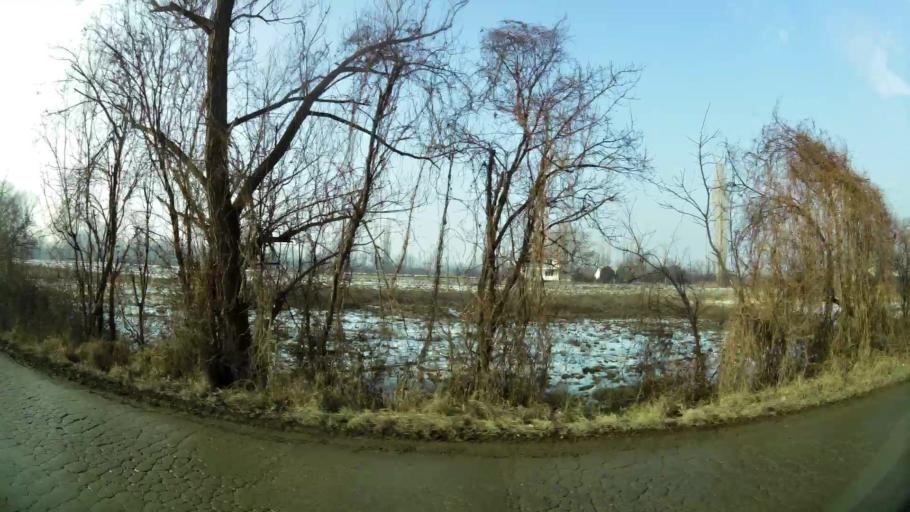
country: MK
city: Kadino
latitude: 41.9617
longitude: 21.5929
